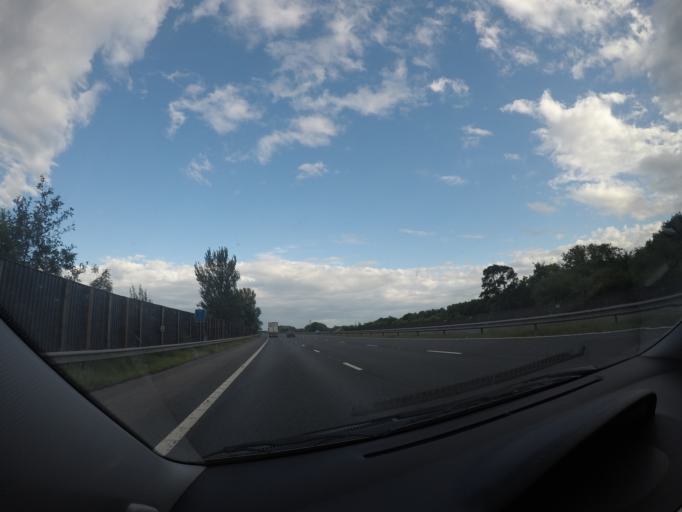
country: GB
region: England
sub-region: Cumbria
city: Carlisle
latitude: 54.9589
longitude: -2.9891
